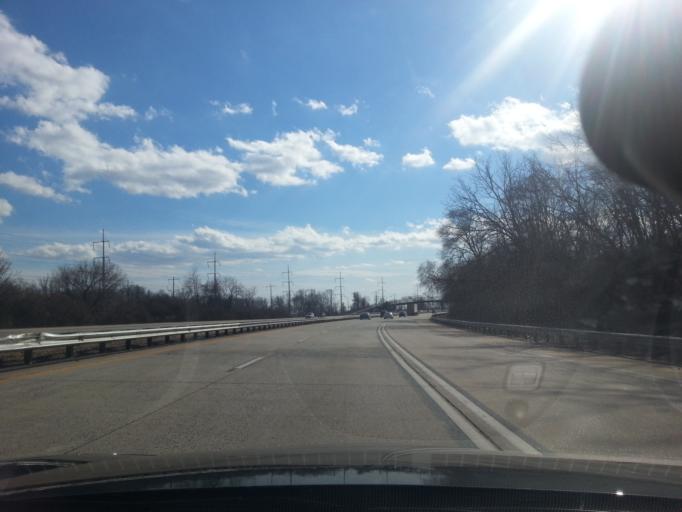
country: US
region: Delaware
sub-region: New Castle County
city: Claymont
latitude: 39.8002
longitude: -75.4516
